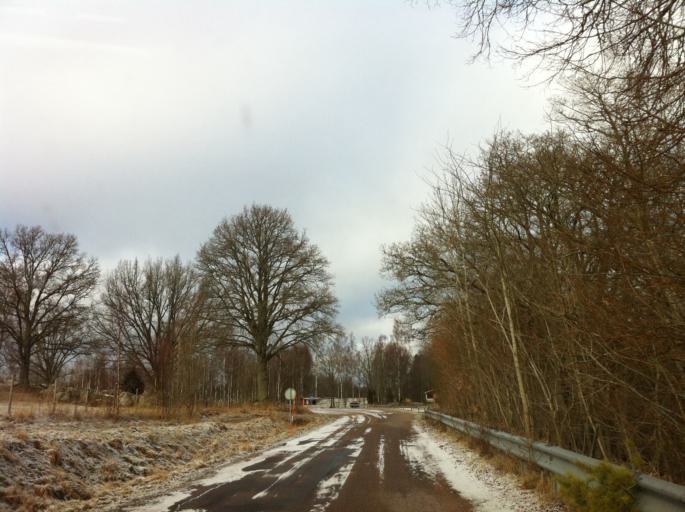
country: SE
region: Joenkoeping
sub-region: Eksjo Kommun
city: Mariannelund
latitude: 57.6134
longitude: 15.6688
